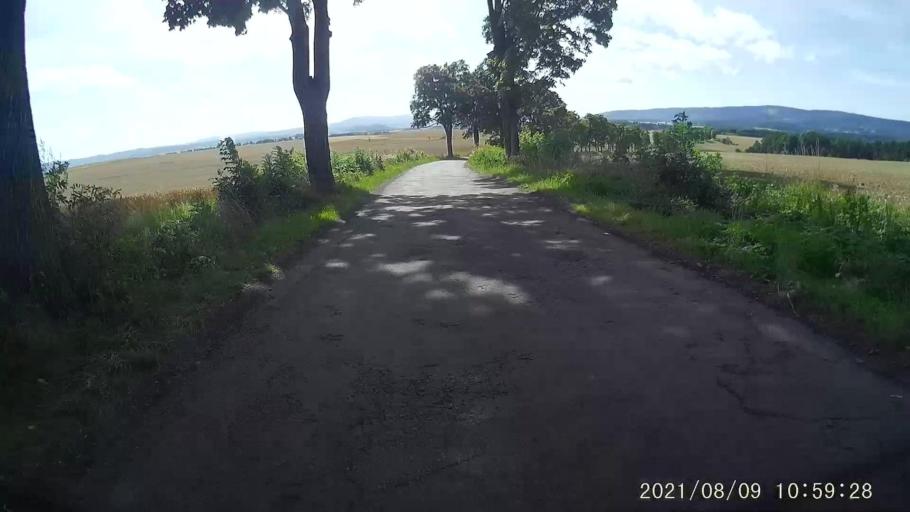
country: PL
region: Lower Silesian Voivodeship
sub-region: Powiat klodzki
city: Polanica-Zdroj
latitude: 50.4493
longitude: 16.5489
